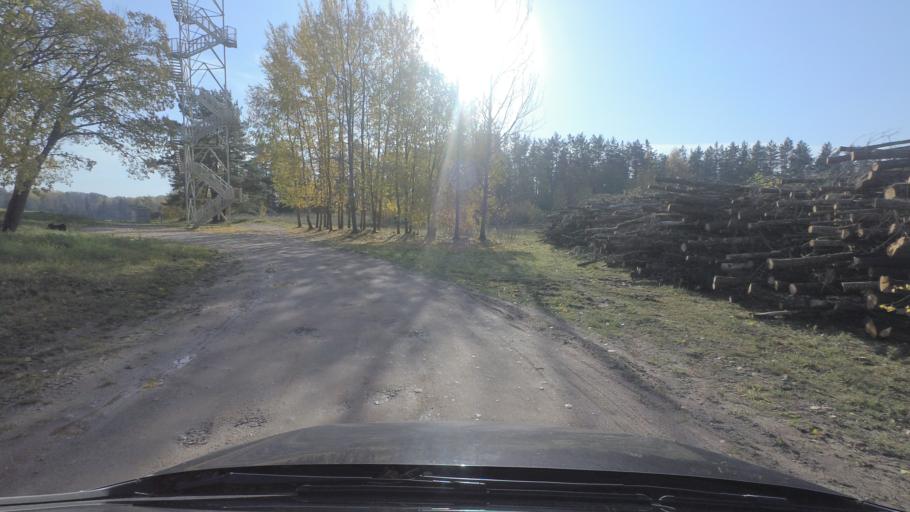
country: LT
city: Ignalina
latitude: 55.3350
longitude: 26.1773
